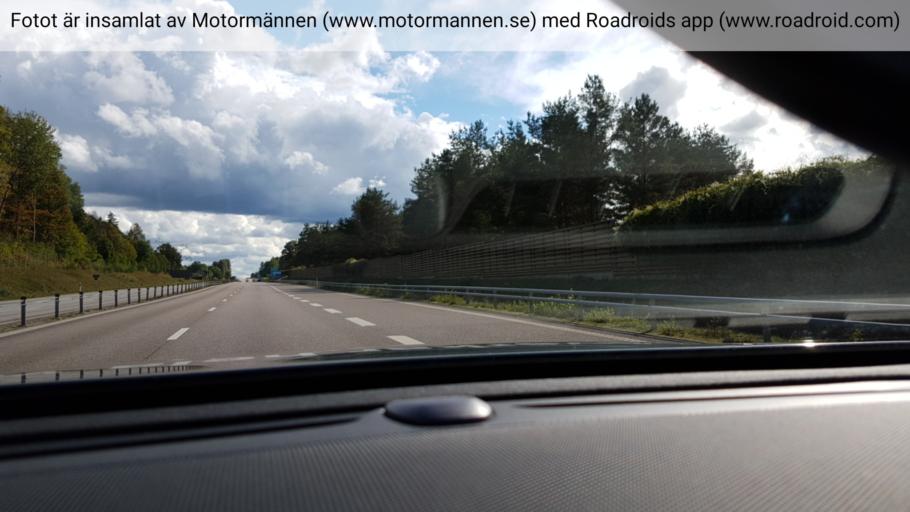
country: SE
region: Vaestra Goetaland
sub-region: Lilla Edets Kommun
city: Lilla Edet
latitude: 58.1411
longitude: 12.1357
